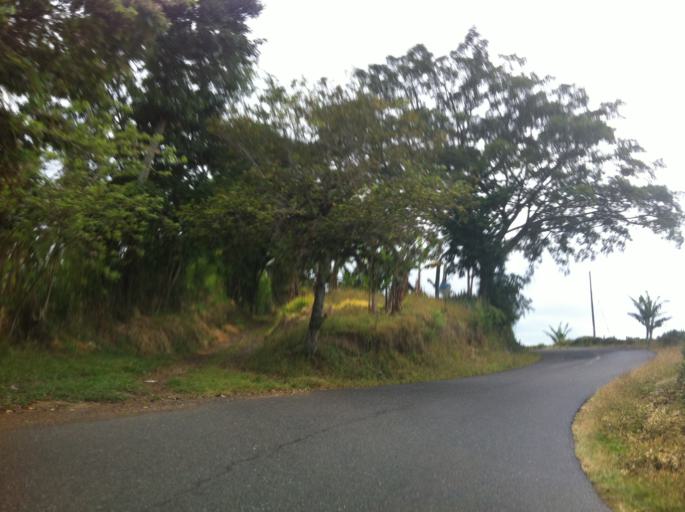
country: CO
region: Quindio
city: Buenavista
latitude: 4.3648
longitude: -75.7471
